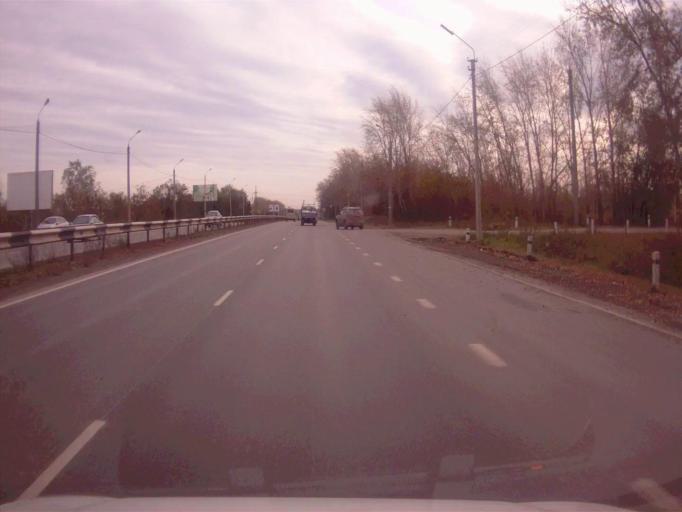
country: RU
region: Chelyabinsk
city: Novosineglazovskiy
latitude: 55.0536
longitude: 61.4094
